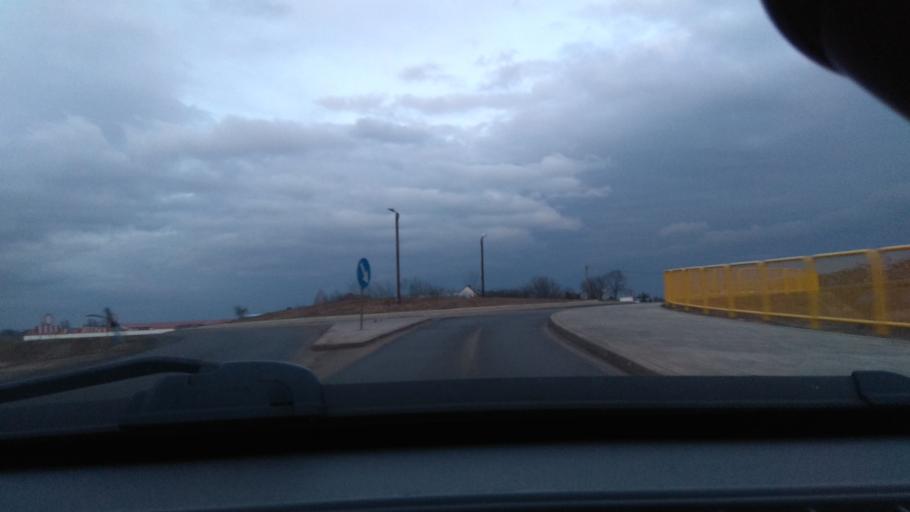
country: PL
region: Greater Poland Voivodeship
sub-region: Powiat kepinski
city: Baranow
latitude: 51.2908
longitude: 18.0241
